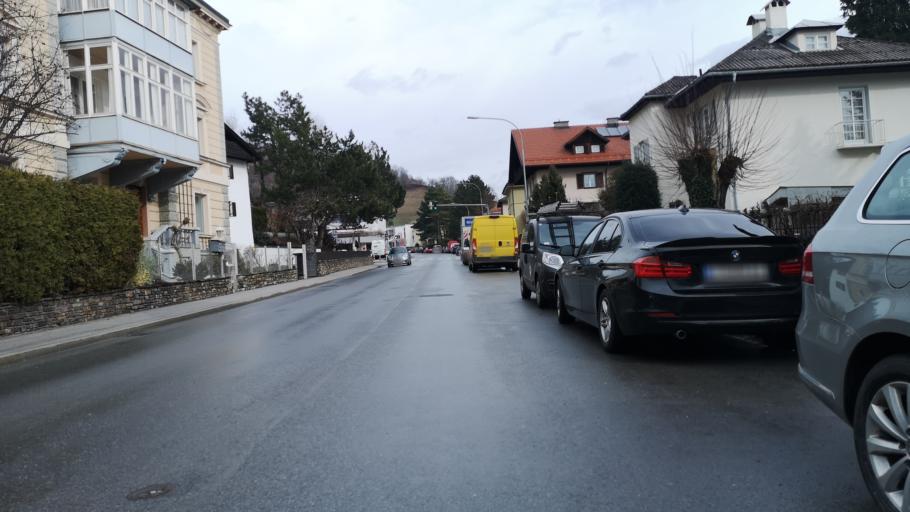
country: AT
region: Tyrol
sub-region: Innsbruck Stadt
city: Innsbruck
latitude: 47.2822
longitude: 11.4090
